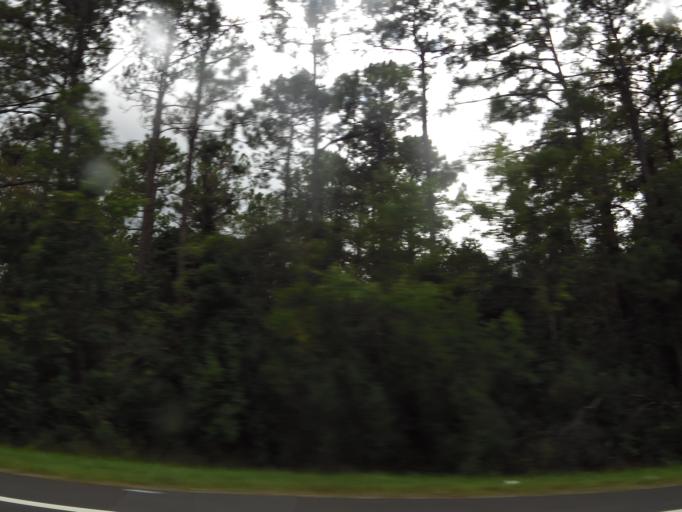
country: US
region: Florida
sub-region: Clay County
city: Asbury Lake
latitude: 30.0421
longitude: -81.8410
